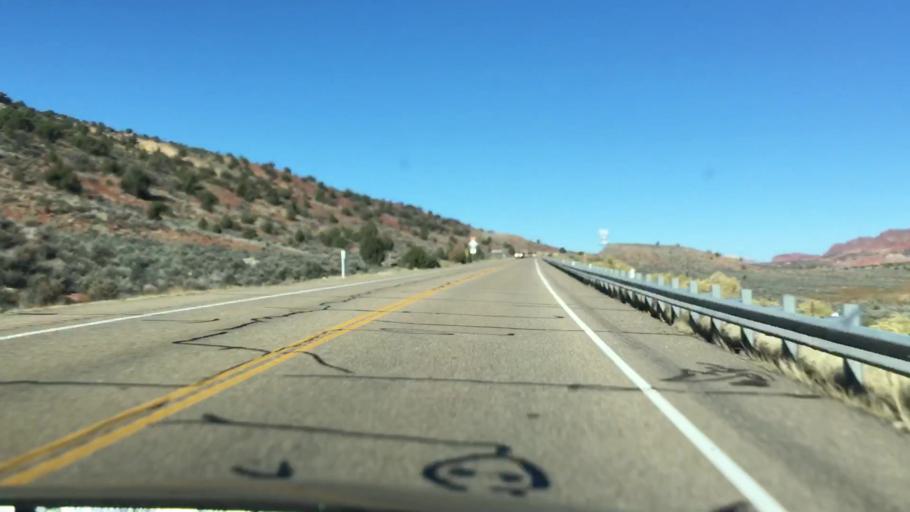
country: US
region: Utah
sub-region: Kane County
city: Kanab
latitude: 37.1268
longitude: -111.9770
